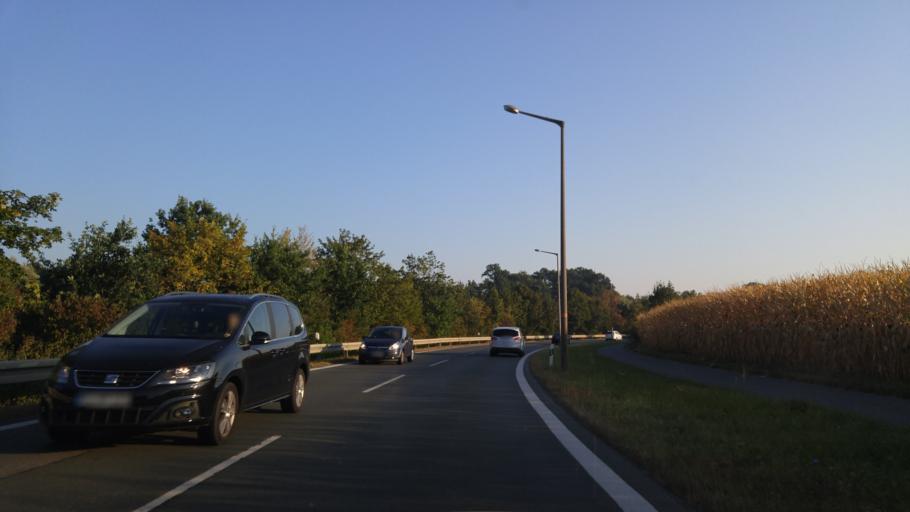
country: DE
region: Bavaria
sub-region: Regierungsbezirk Mittelfranken
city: Furth
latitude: 49.5099
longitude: 10.9572
